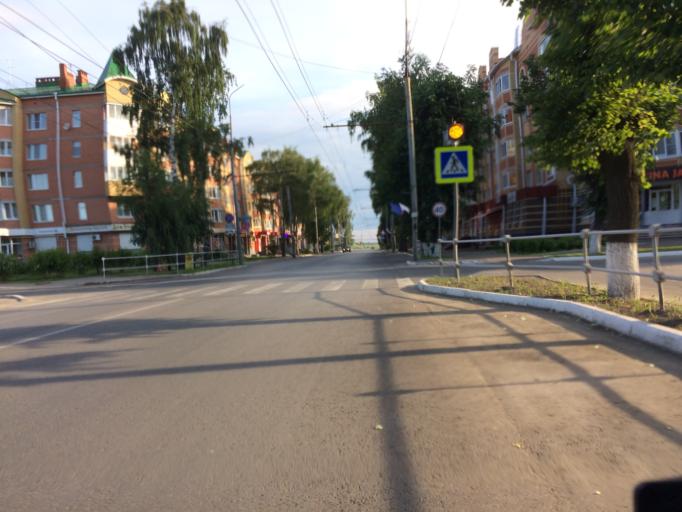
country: RU
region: Mariy-El
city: Medvedevo
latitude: 56.6361
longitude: 47.8032
